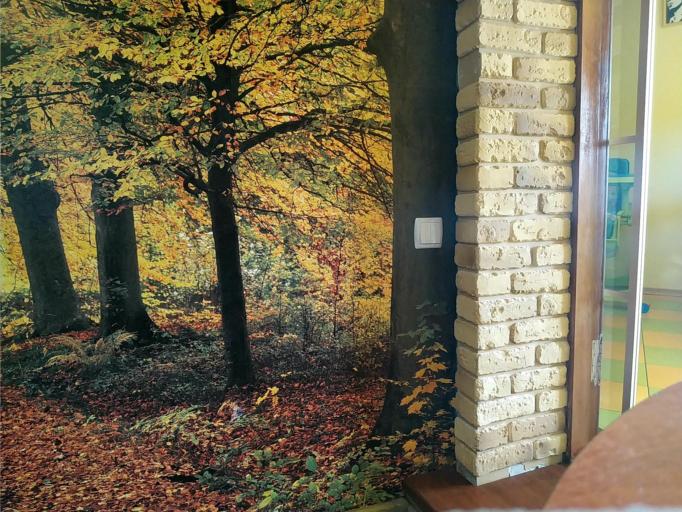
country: RU
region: Smolensk
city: Katyn'
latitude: 54.9620
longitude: 31.7243
